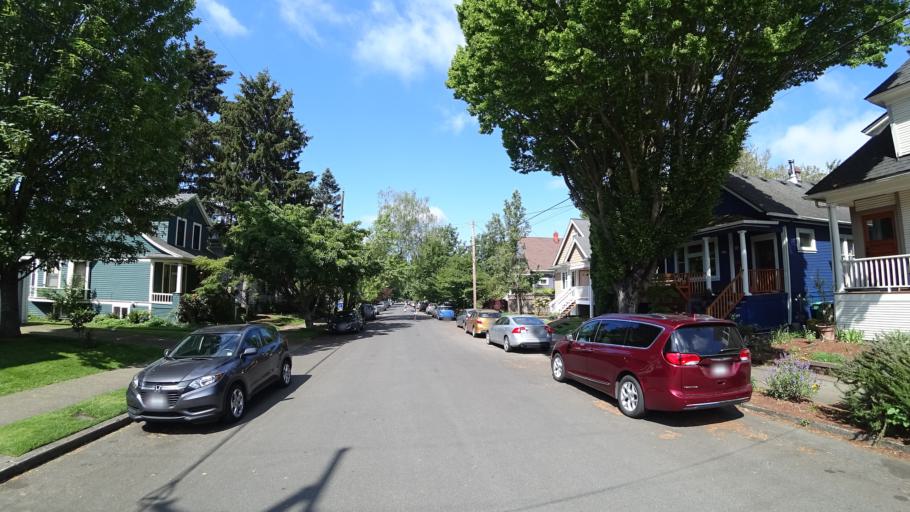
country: US
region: Oregon
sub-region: Multnomah County
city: Portland
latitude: 45.5136
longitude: -122.6426
